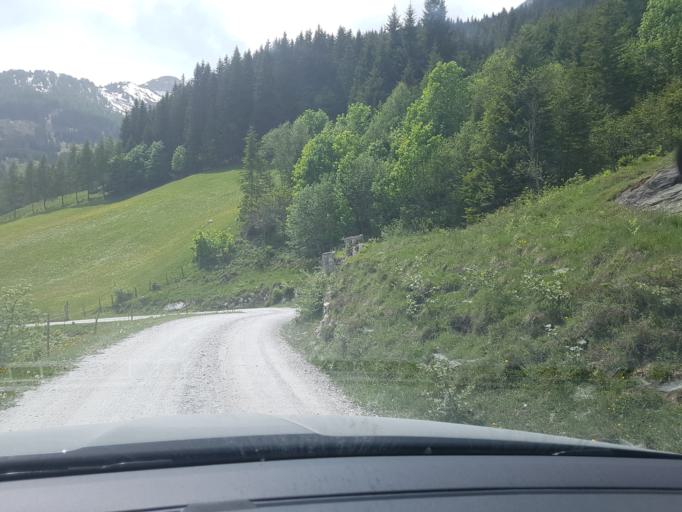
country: AT
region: Salzburg
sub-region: Politischer Bezirk Sankt Johann im Pongau
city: Schwarzach im Pongau
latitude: 47.2768
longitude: 13.1952
